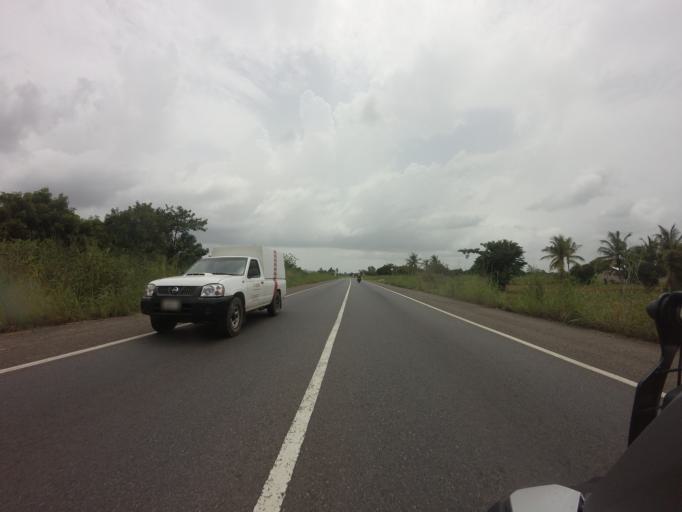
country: GH
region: Volta
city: Keta
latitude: 6.0762
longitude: 0.8548
